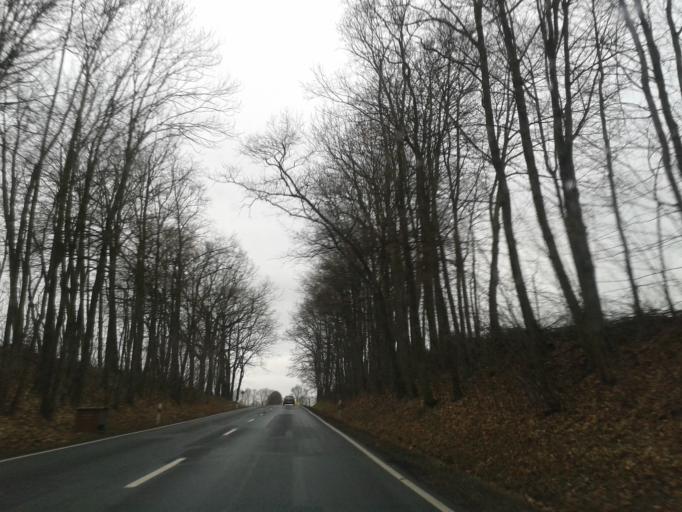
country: DE
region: Saxony
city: Grossschweidnitz
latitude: 51.0717
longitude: 14.6515
